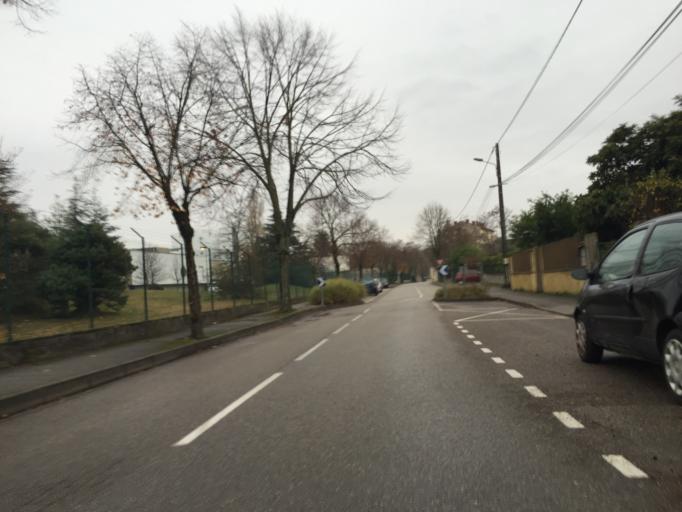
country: FR
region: Rhone-Alpes
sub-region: Departement de l'Ain
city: Saint-Maurice-de-Beynost
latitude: 45.8248
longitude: 4.9772
